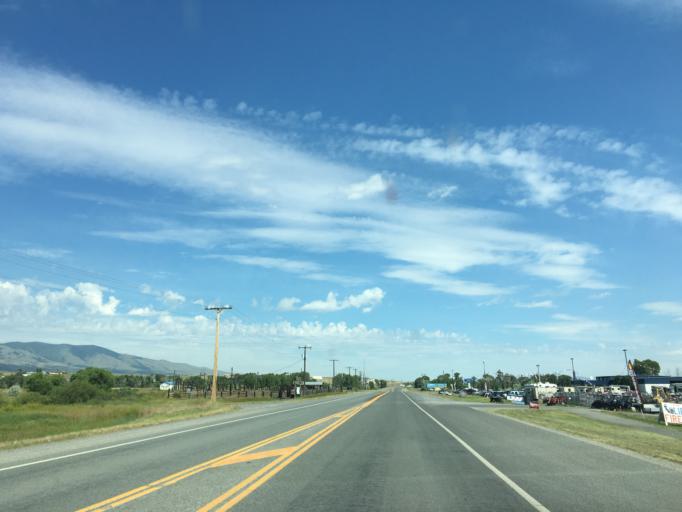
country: US
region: Montana
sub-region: Broadwater County
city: Townsend
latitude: 46.3275
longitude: -111.5269
